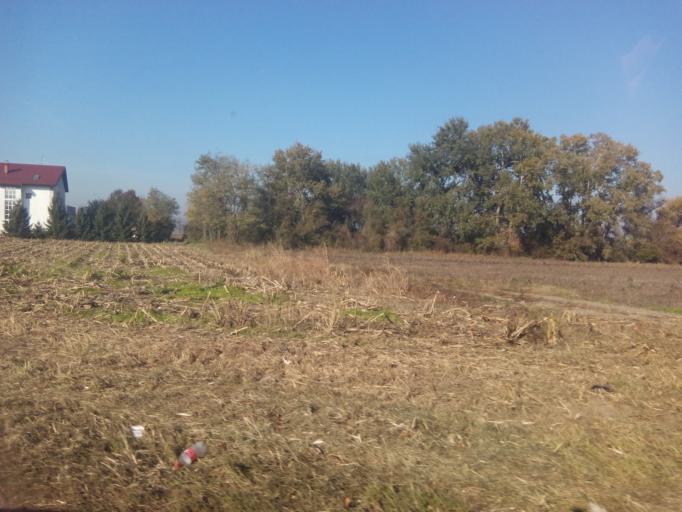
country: RS
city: Glozan
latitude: 45.2740
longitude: 19.5483
